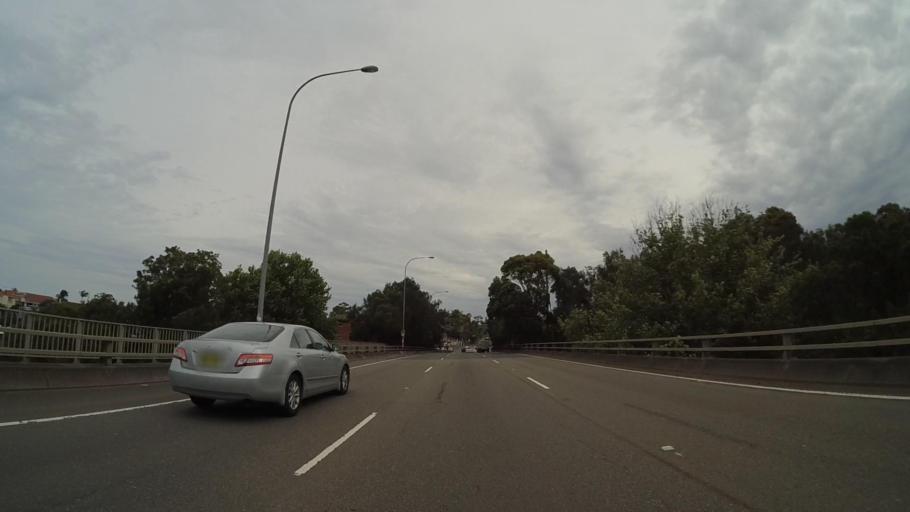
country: AU
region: New South Wales
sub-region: Kogarah
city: Blakehurst
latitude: -34.0056
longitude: 151.1126
